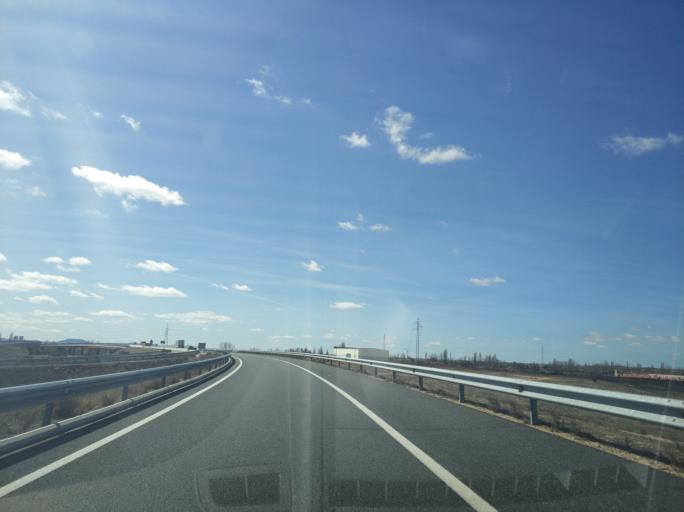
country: ES
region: Castille and Leon
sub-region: Provincia de Valladolid
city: Cabezon
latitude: 41.7334
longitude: -4.6761
